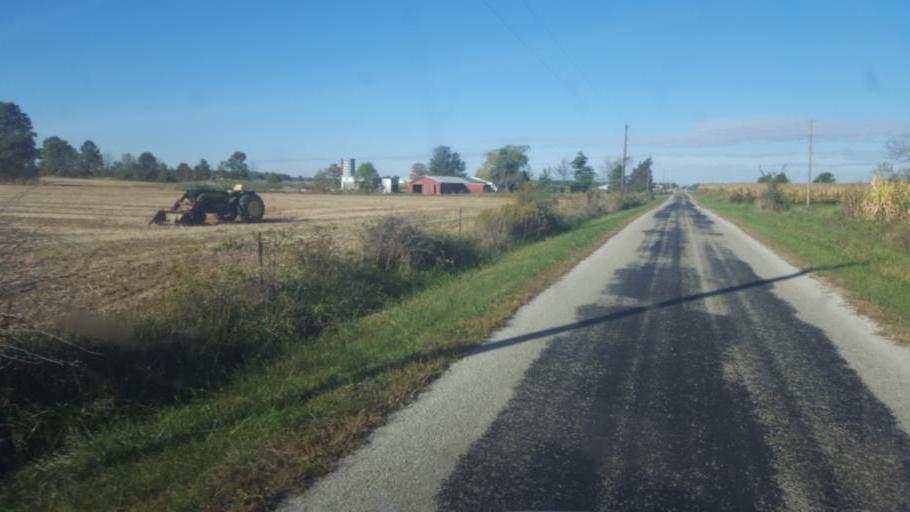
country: US
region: Ohio
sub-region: Crawford County
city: Galion
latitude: 40.6900
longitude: -82.9014
